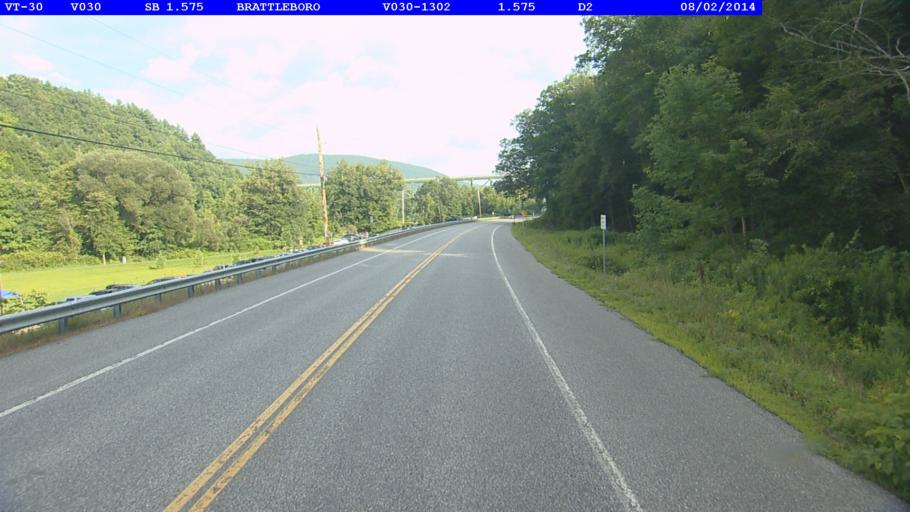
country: US
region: Vermont
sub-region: Windham County
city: Brattleboro
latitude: 42.8773
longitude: -72.5740
